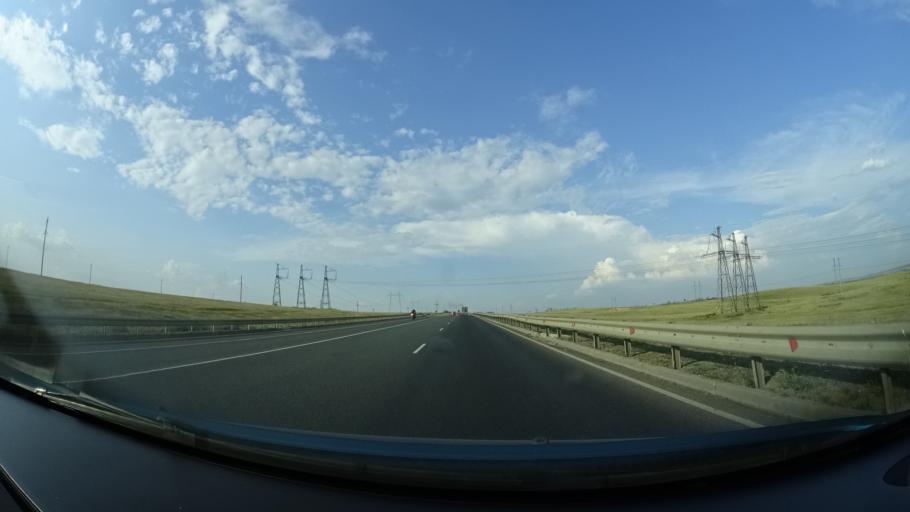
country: RU
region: Samara
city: Sukhodol
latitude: 53.7006
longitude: 50.8050
